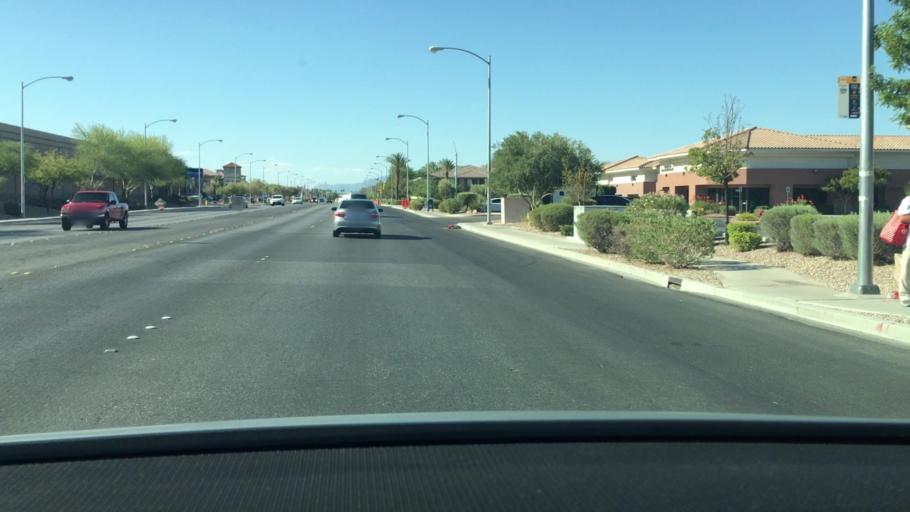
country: US
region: Nevada
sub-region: Clark County
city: Summerlin South
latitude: 36.0874
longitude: -115.2974
